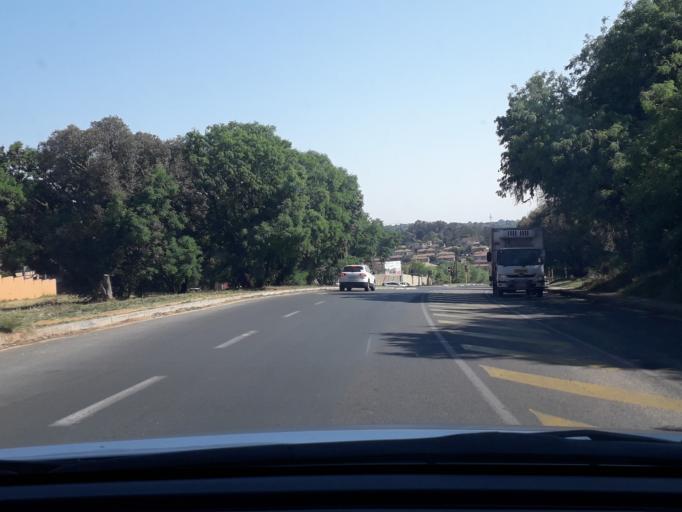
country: ZA
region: Gauteng
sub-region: City of Johannesburg Metropolitan Municipality
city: Roodepoort
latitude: -26.0844
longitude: 27.9573
